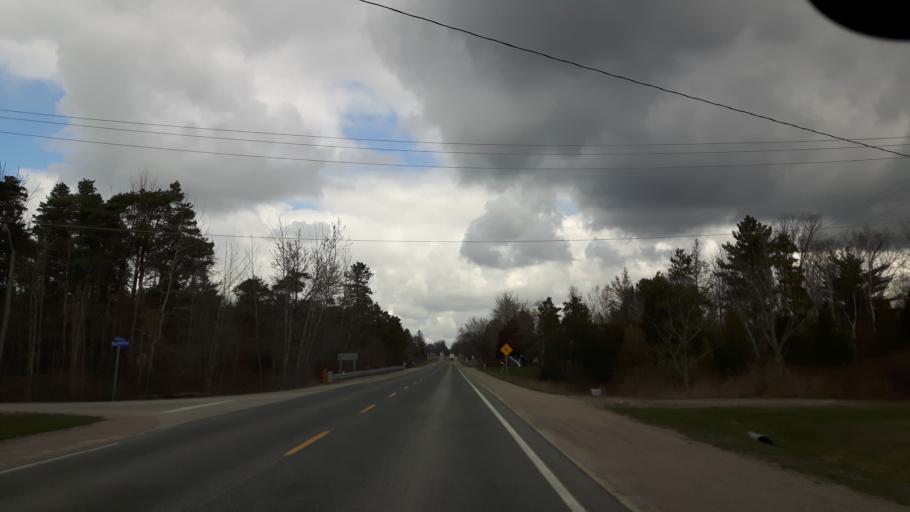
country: CA
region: Ontario
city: Bluewater
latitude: 43.5488
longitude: -81.6904
